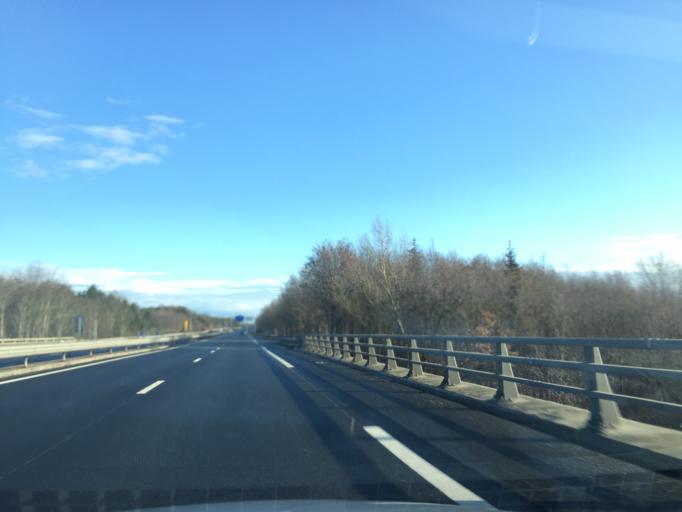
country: FR
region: Rhone-Alpes
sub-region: Departement de la Loire
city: Saint-Germain-Laval
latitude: 45.8587
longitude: 4.0327
